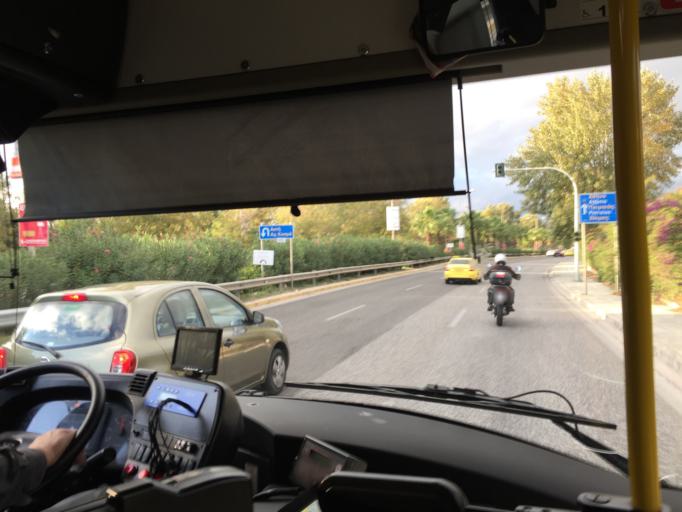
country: GR
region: Attica
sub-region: Nomarchia Athinas
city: Elliniko
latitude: 37.8928
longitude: 23.7223
